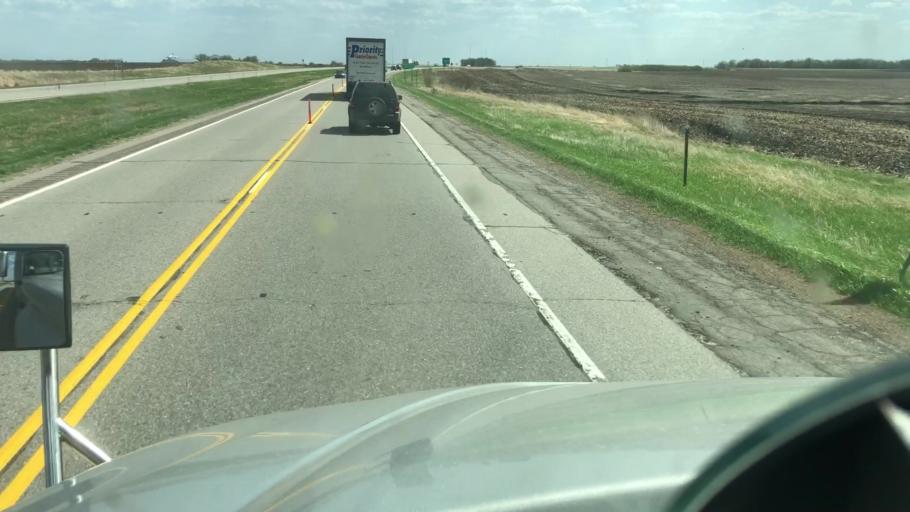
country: US
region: Minnesota
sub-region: Scott County
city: Belle Plaine
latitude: 44.5536
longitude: -93.8503
